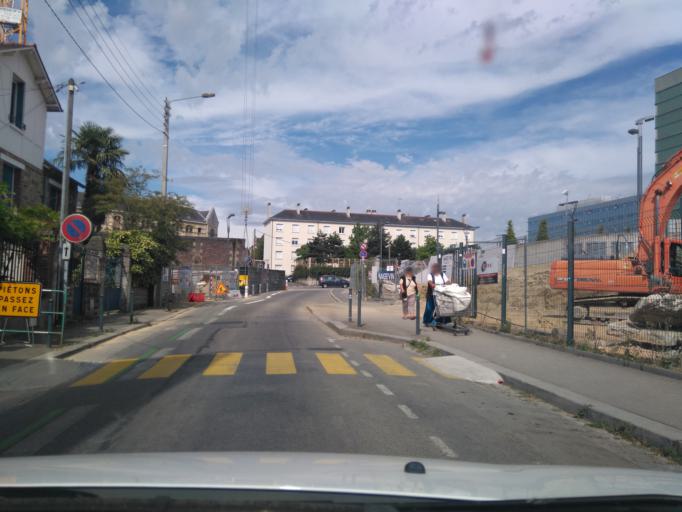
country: FR
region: Brittany
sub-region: Departement d'Ille-et-Vilaine
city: Rennes
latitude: 48.1015
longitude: -1.6717
